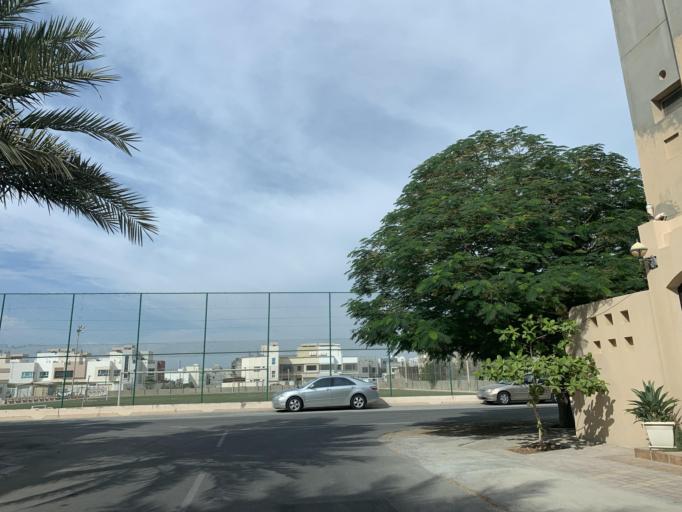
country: BH
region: Central Governorate
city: Madinat Hamad
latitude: 26.1178
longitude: 50.4770
